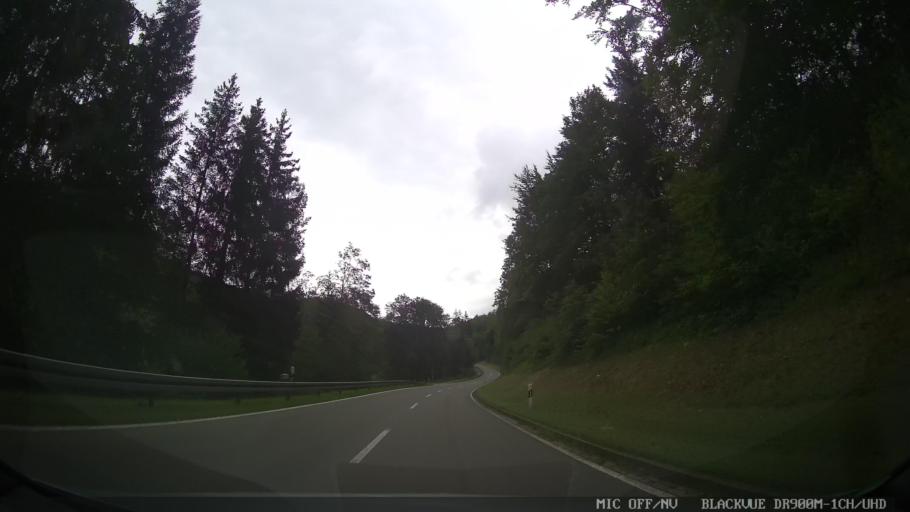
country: DE
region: Baden-Wuerttemberg
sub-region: Freiburg Region
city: Barenthal
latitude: 48.0447
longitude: 8.9309
